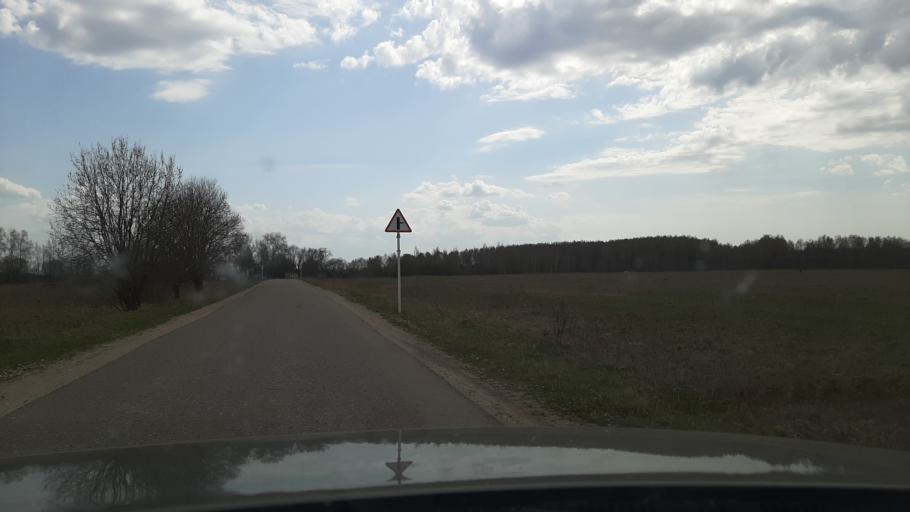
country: RU
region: Ivanovo
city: Furmanov
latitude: 57.3052
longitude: 41.1615
